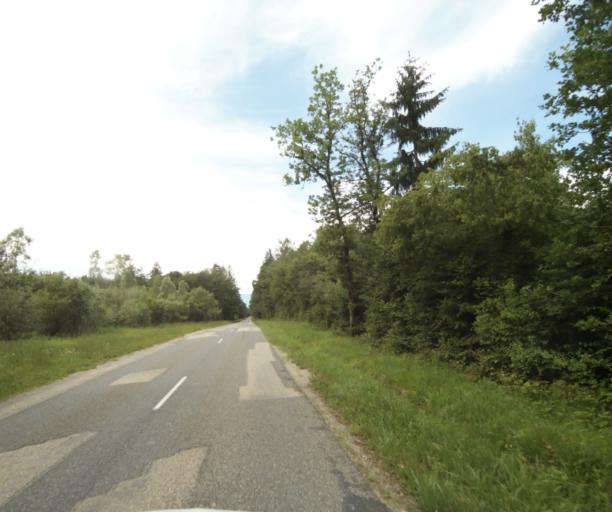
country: FR
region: Rhone-Alpes
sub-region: Departement de la Haute-Savoie
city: Sciez
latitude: 46.3088
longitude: 6.4076
